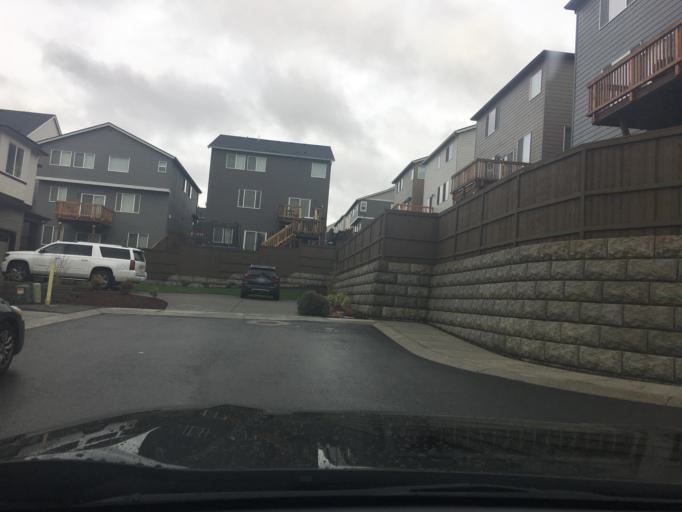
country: US
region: Oregon
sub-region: Washington County
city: Bethany
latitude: 45.5708
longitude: -122.8542
